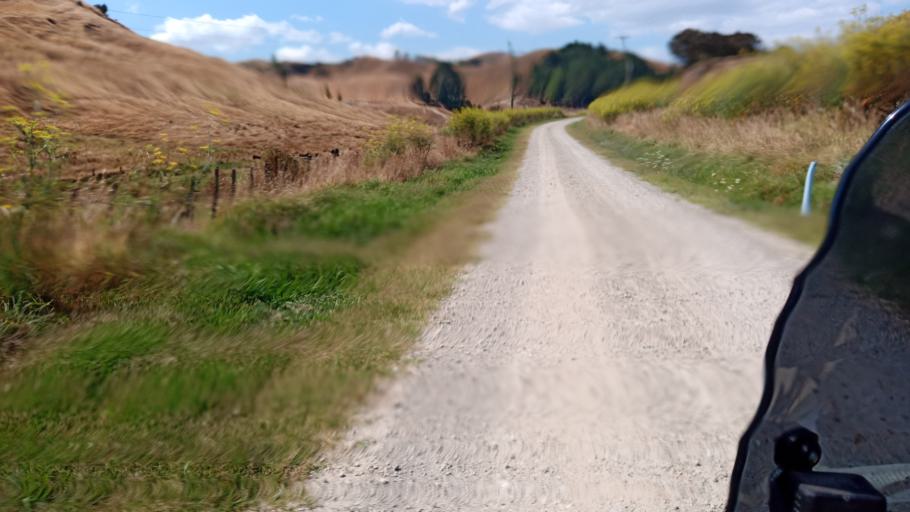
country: NZ
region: Gisborne
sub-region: Gisborne District
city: Gisborne
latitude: -38.4883
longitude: 177.8465
